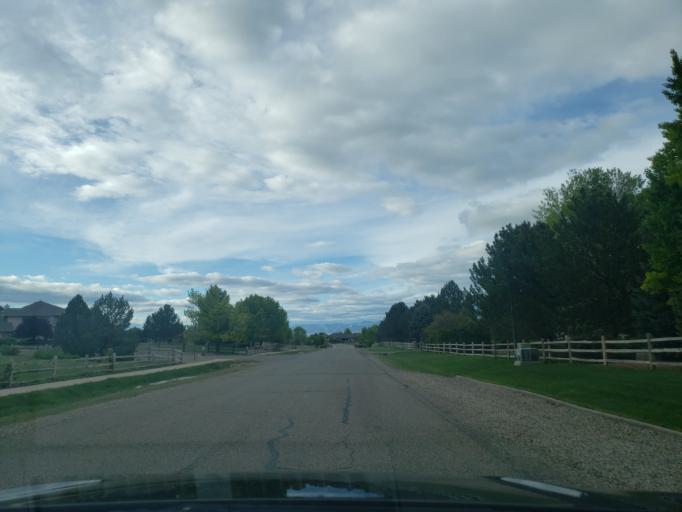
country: US
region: Colorado
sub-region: Mesa County
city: Redlands
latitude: 39.1043
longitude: -108.6746
